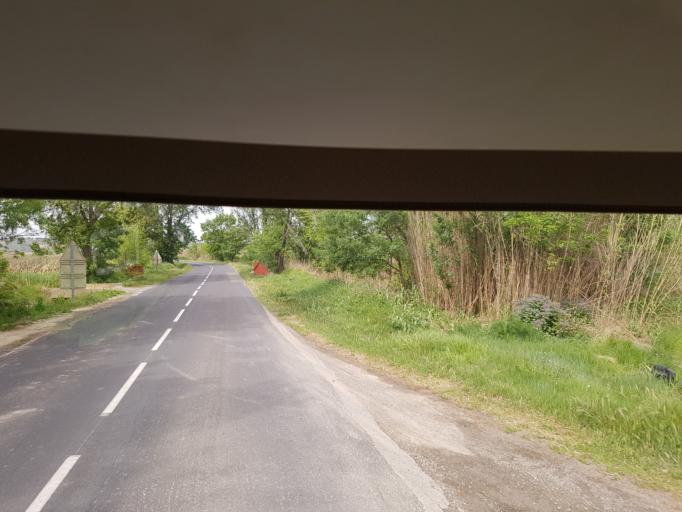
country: FR
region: Languedoc-Roussillon
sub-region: Departement de l'Aude
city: Fleury
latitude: 43.2494
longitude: 3.1545
